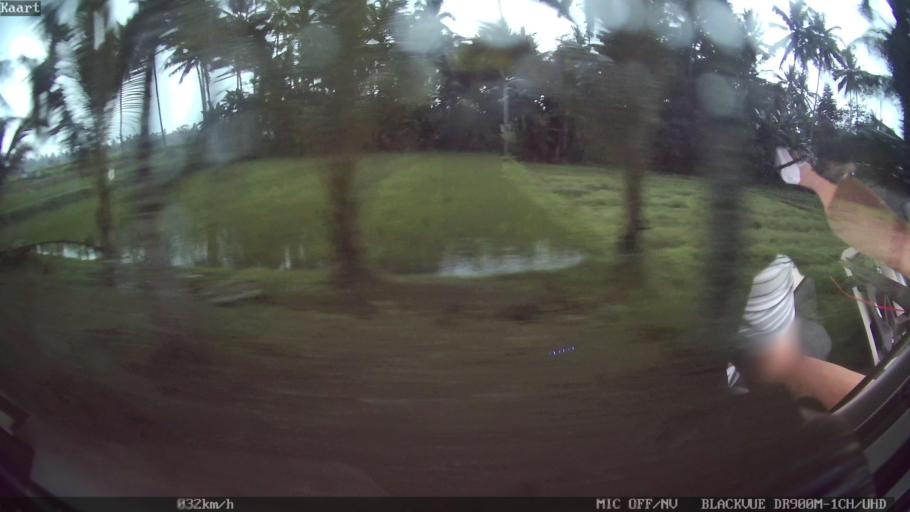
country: ID
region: Bali
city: Kekeran
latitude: -8.4889
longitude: 115.1877
